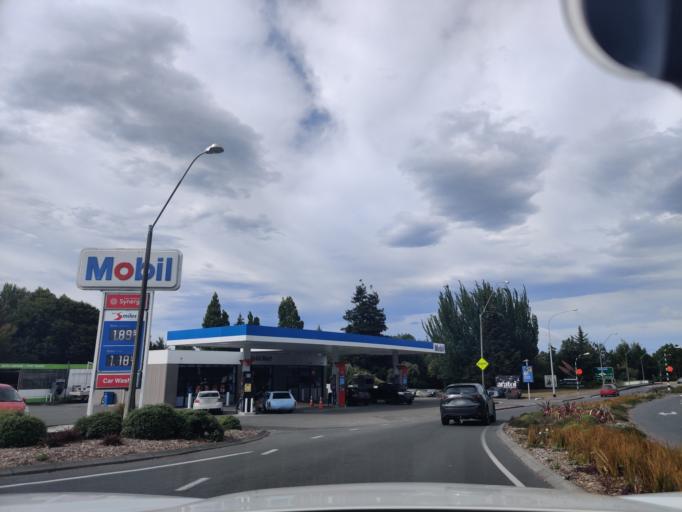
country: NZ
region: Wellington
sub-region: Masterton District
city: Masterton
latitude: -40.9449
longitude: 175.6693
